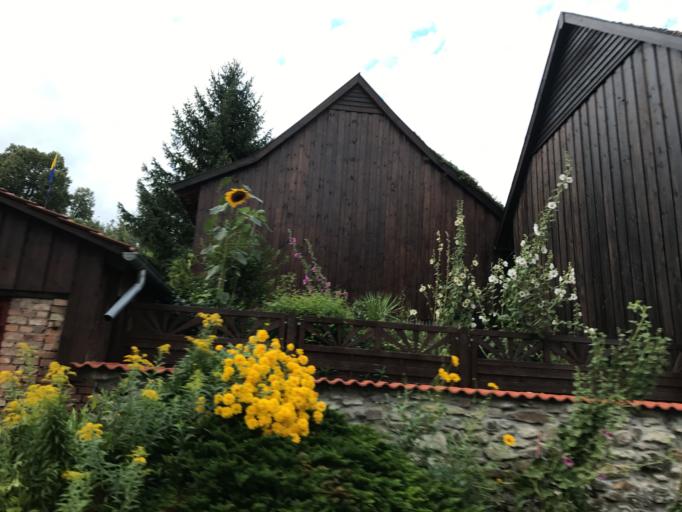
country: DE
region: Saxony-Anhalt
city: Stapelburg
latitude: 51.9028
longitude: 10.6687
